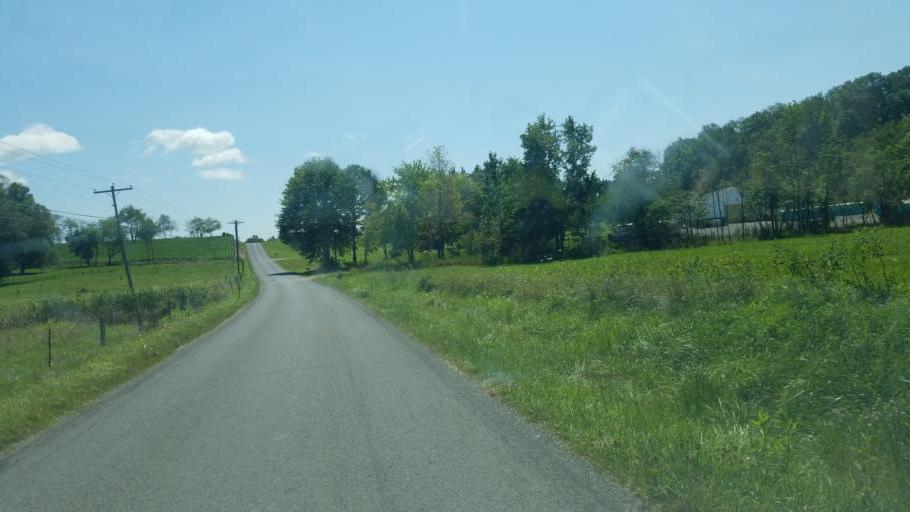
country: US
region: Pennsylvania
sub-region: Clarion County
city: Knox
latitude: 41.2128
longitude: -79.5380
